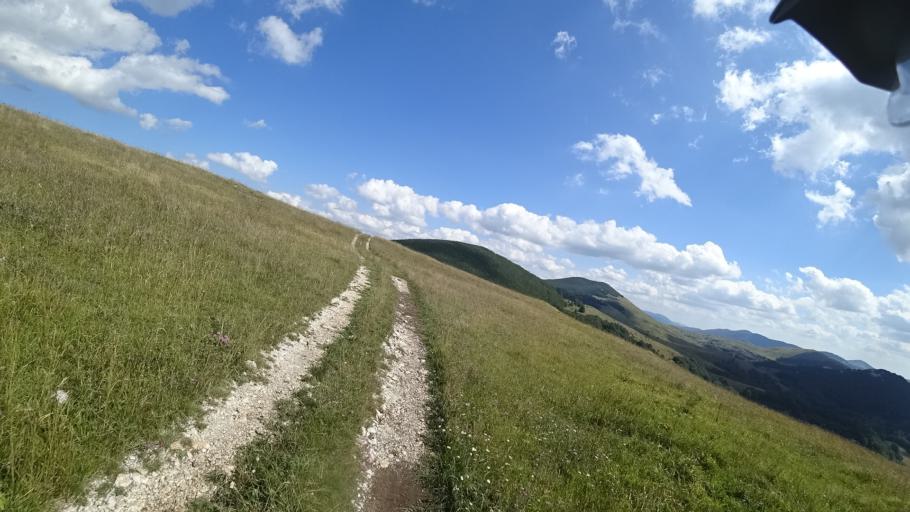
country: HR
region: Zadarska
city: Gracac
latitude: 44.4298
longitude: 15.9911
